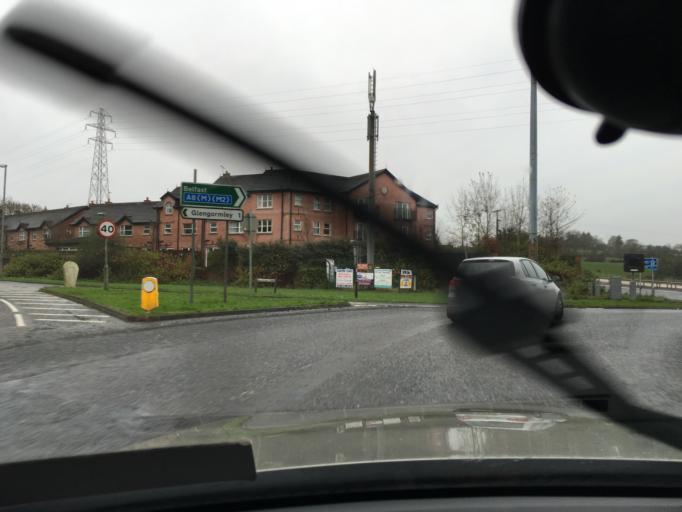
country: GB
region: Northern Ireland
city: Carnmoney
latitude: 54.6924
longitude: -5.9702
